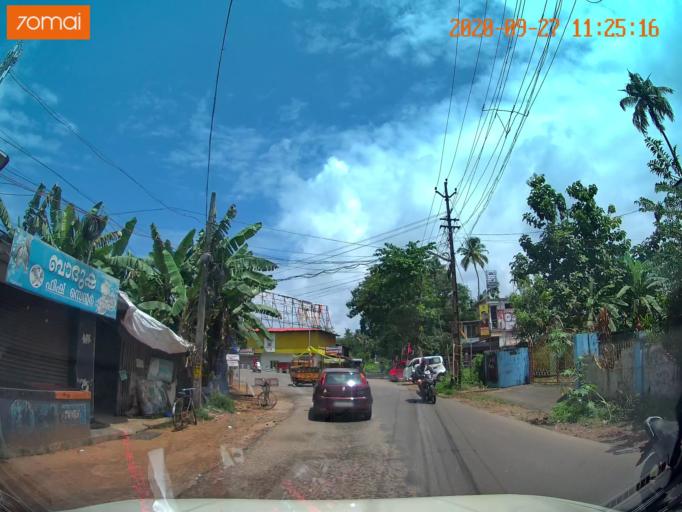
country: IN
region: Kerala
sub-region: Thrissur District
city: Thanniyam
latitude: 10.4134
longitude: 76.1581
